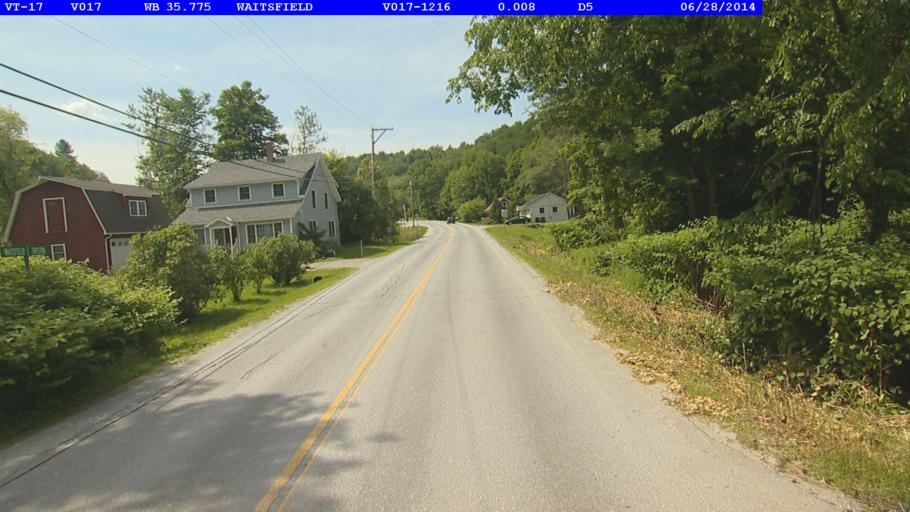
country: US
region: Vermont
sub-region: Washington County
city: Waterbury
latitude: 44.1811
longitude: -72.8434
